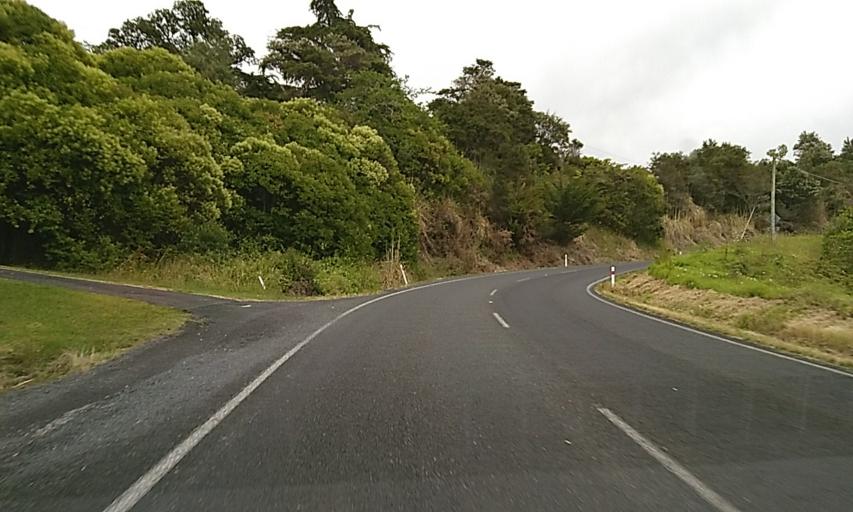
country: NZ
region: Auckland
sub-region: Auckland
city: Pukekohe East
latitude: -37.2987
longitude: 174.9434
